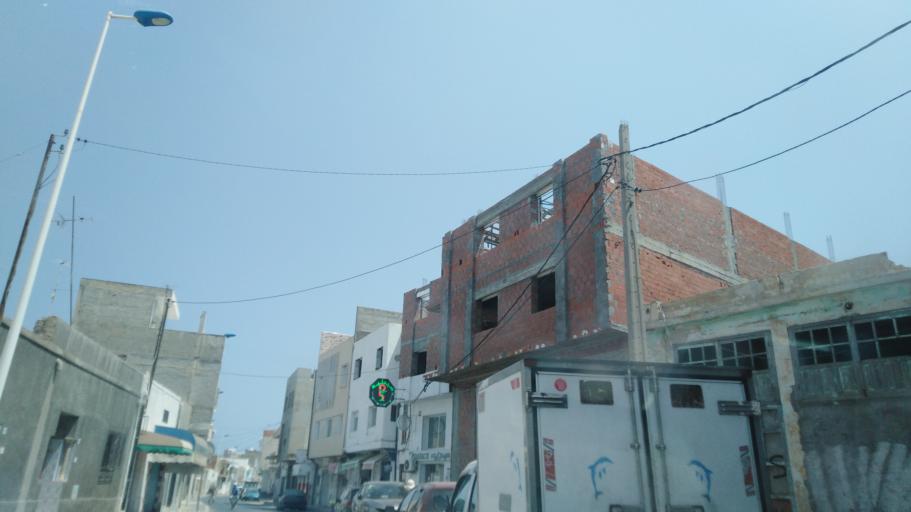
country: TN
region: Al Mahdiyah
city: Mahdia
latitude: 35.5138
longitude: 11.0425
